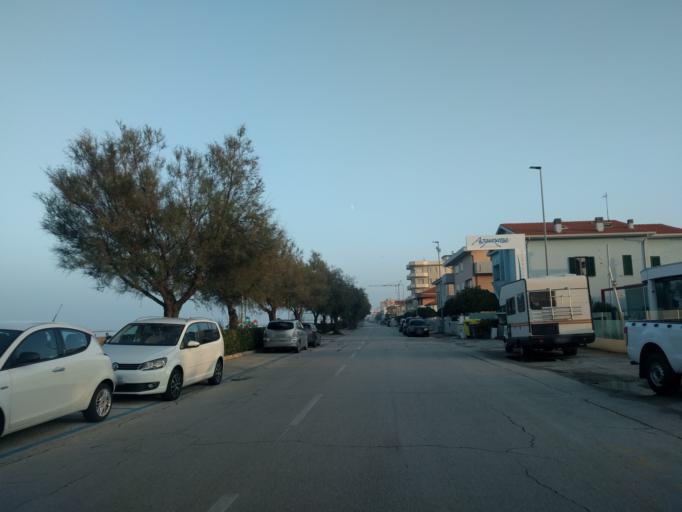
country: IT
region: The Marches
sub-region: Provincia di Ancona
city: Senigallia
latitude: 43.7316
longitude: 13.1990
